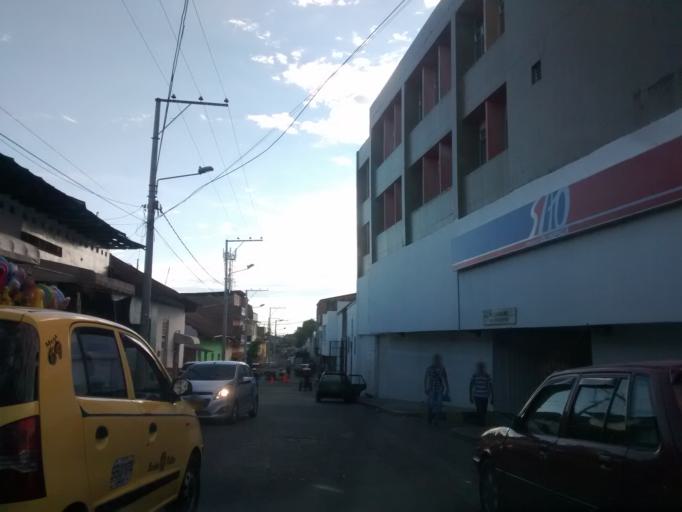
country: CO
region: Cundinamarca
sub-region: Girardot
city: Girardot City
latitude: 4.2932
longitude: -74.8061
